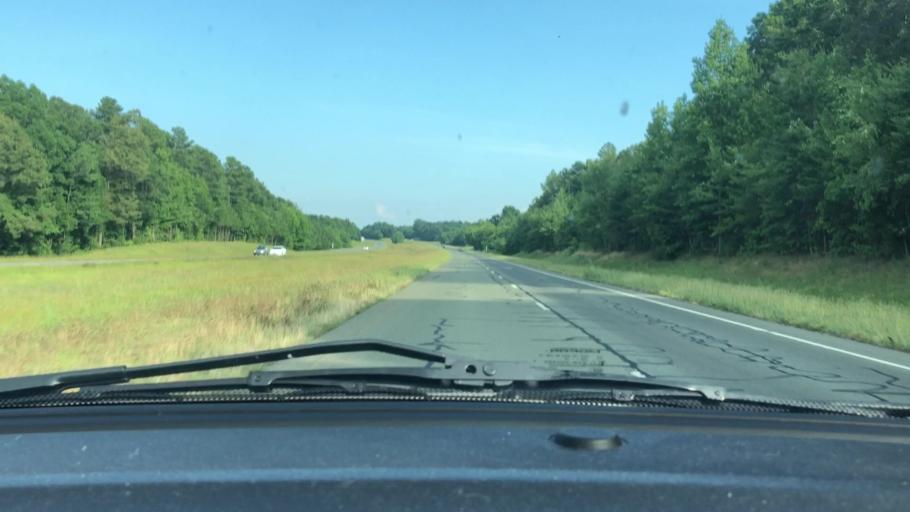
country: US
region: North Carolina
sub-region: Randolph County
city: Liberty
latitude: 35.7963
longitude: -79.5337
